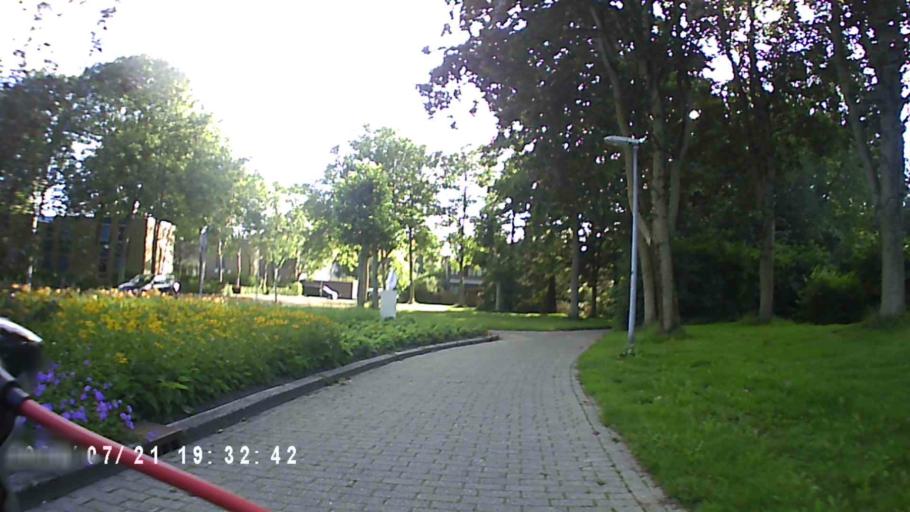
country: NL
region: Groningen
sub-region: Gemeente Groningen
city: Oosterpark
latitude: 53.2390
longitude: 6.6163
